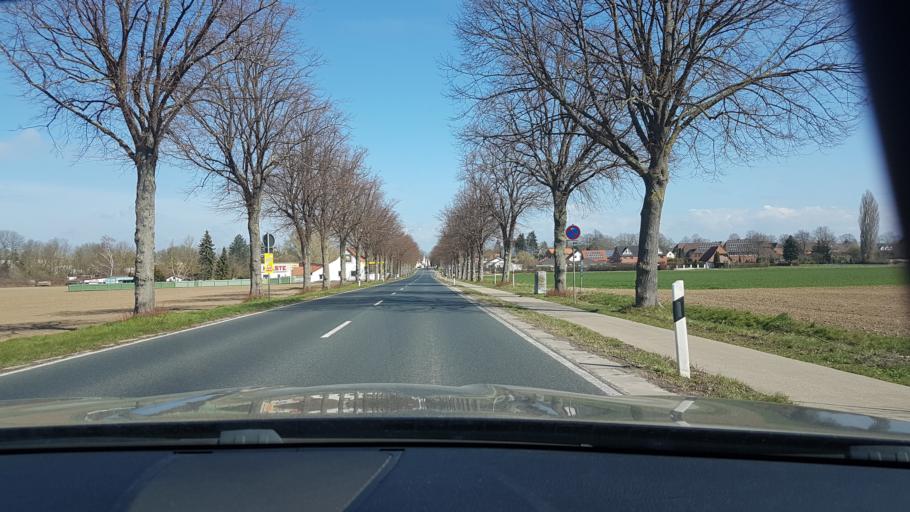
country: DE
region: Lower Saxony
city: Pattensen
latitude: 52.2548
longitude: 9.7574
